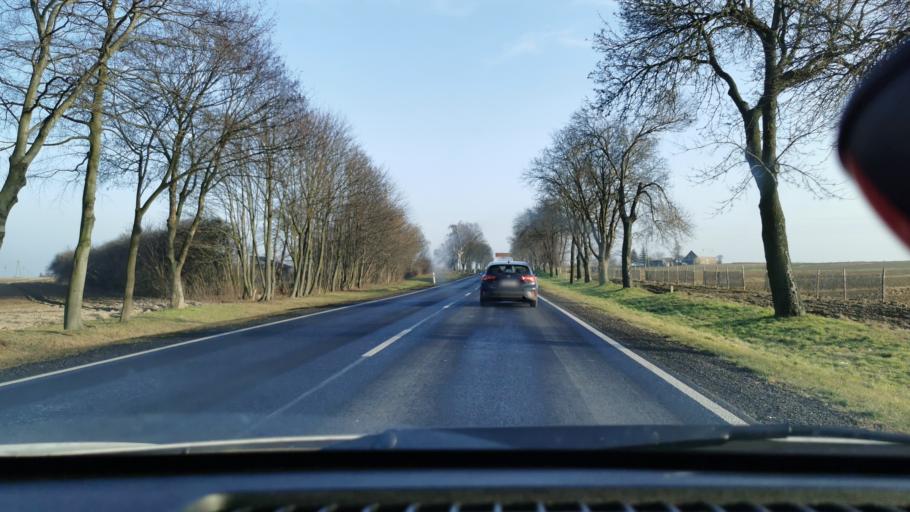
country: PL
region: Lodz Voivodeship
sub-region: Powiat sieradzki
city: Wroblew
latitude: 51.6186
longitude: 18.5919
